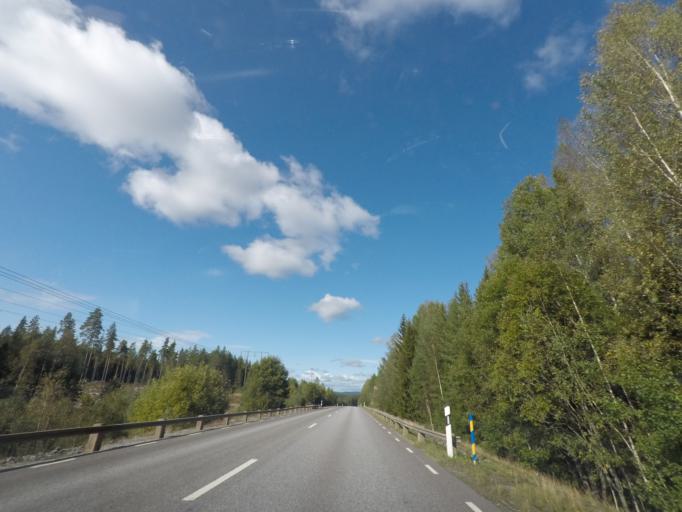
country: SE
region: Vaestmanland
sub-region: Skinnskattebergs Kommun
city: Skinnskatteberg
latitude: 59.8519
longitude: 15.6633
